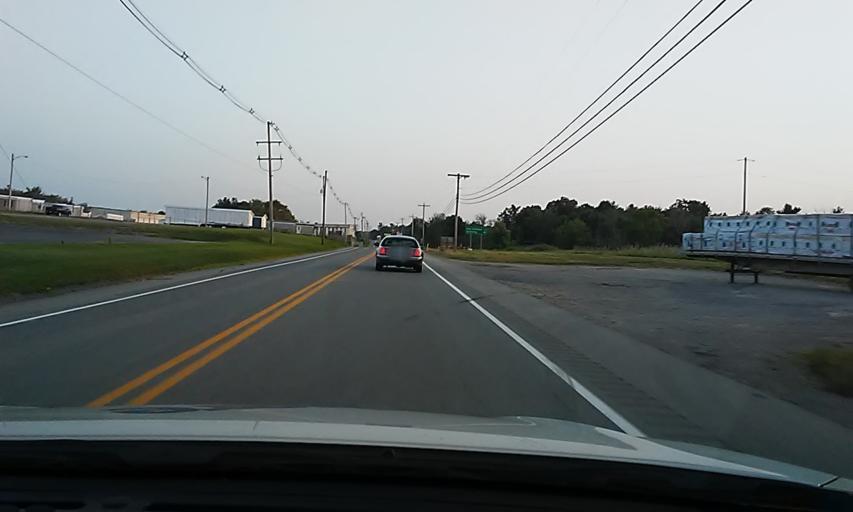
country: US
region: Pennsylvania
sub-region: Clarion County
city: Marianne
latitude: 41.2368
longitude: -79.4291
